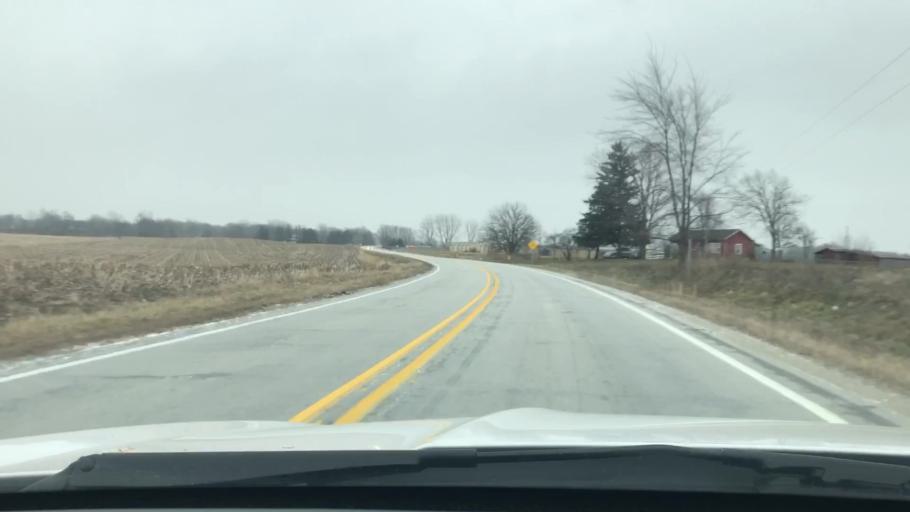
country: US
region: Indiana
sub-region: Fulton County
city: Akron
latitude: 41.0402
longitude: -86.0854
